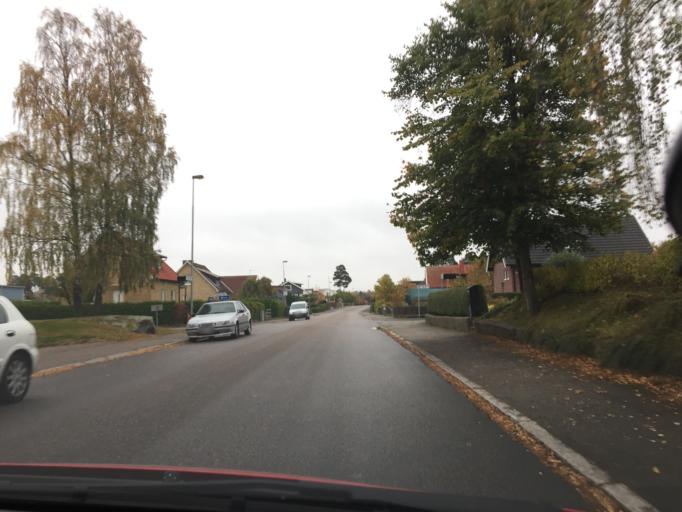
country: SE
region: Vaestra Goetaland
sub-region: Trollhattan
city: Trollhattan
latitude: 58.2835
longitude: 12.3123
